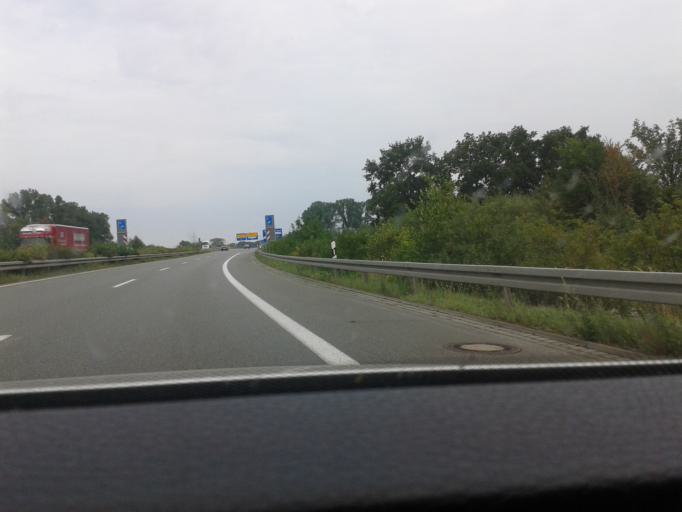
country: DE
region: Lower Saxony
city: Tappenbeck
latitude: 52.4579
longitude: 10.7361
